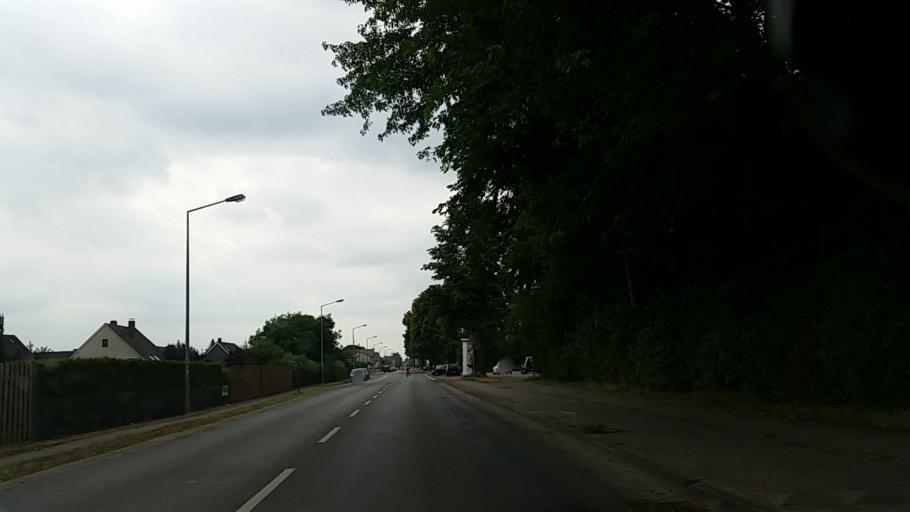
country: DE
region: Lower Saxony
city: Ruhen
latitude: 52.4508
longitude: 10.8494
